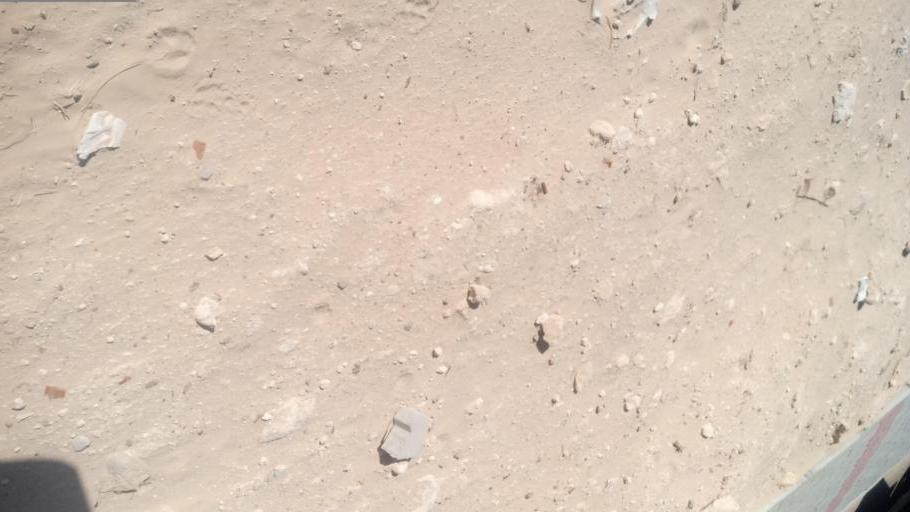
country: TN
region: Qibili
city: Douz
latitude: 33.4594
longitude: 9.0504
